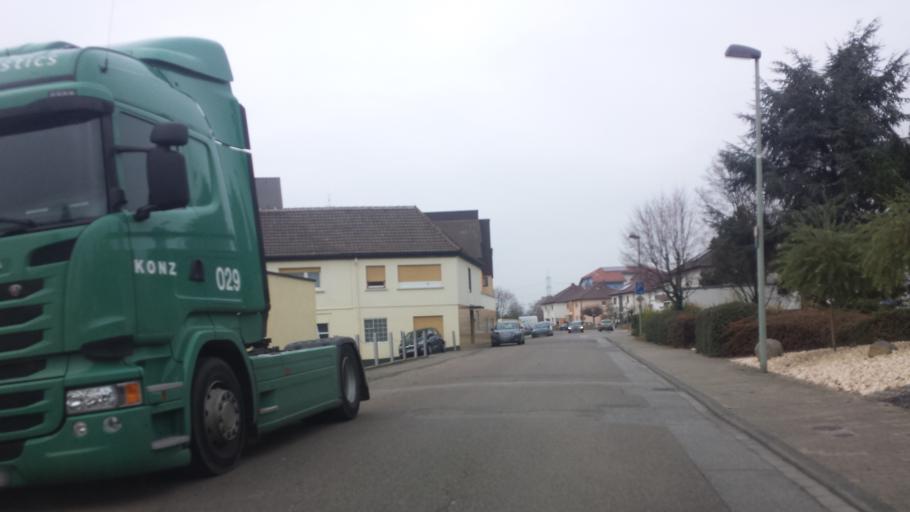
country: DE
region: Hesse
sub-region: Regierungsbezirk Darmstadt
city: Burstadt
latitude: 49.6414
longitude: 8.4495
